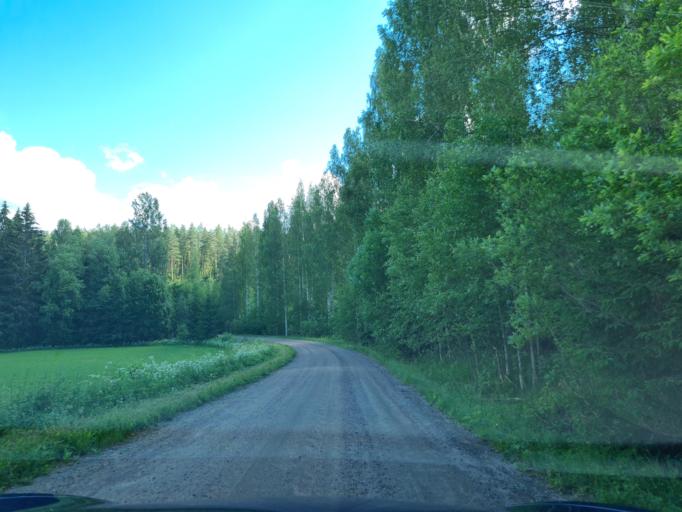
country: FI
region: Uusimaa
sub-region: Helsinki
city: Kaerkoelae
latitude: 60.7546
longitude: 23.9449
